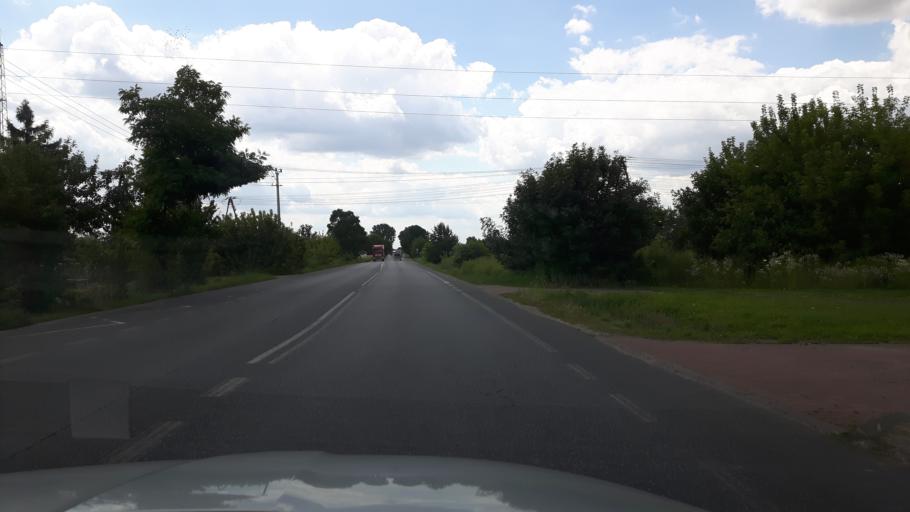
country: PL
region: Masovian Voivodeship
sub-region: Powiat wyszkowski
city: Wyszkow
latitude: 52.6195
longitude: 21.4923
